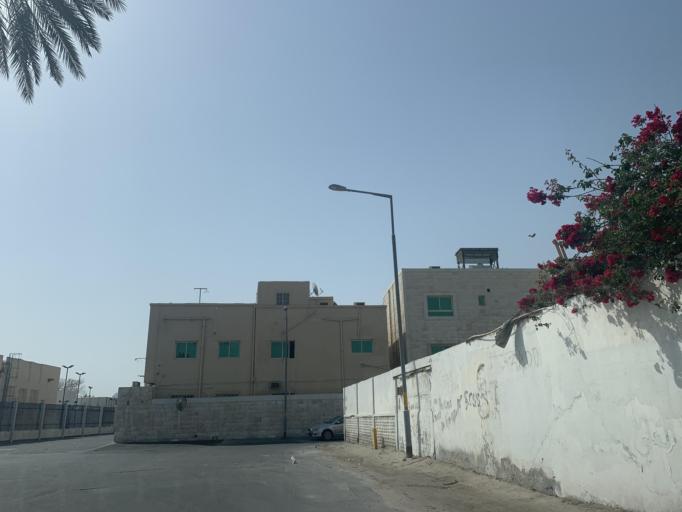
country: BH
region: Manama
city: Manama
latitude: 26.2233
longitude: 50.5666
